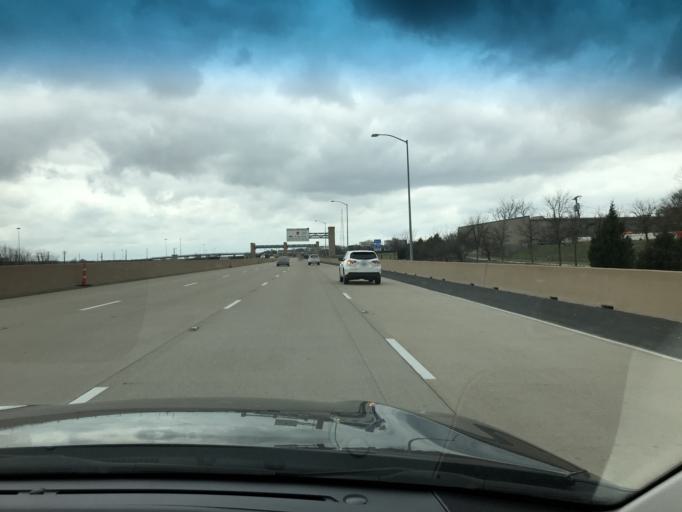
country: US
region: Texas
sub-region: Tarrant County
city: Westworth
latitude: 32.7276
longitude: -97.3741
